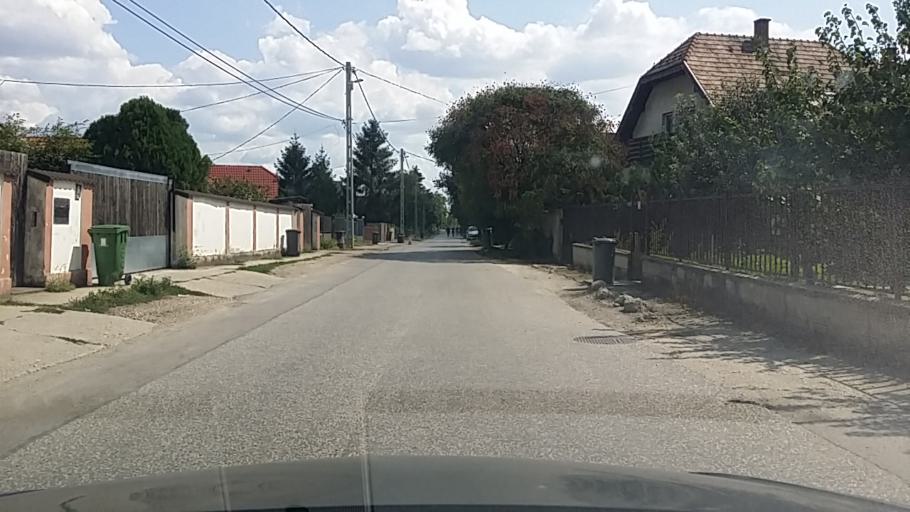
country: HU
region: Pest
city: Halasztelek
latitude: 47.3815
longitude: 19.0116
